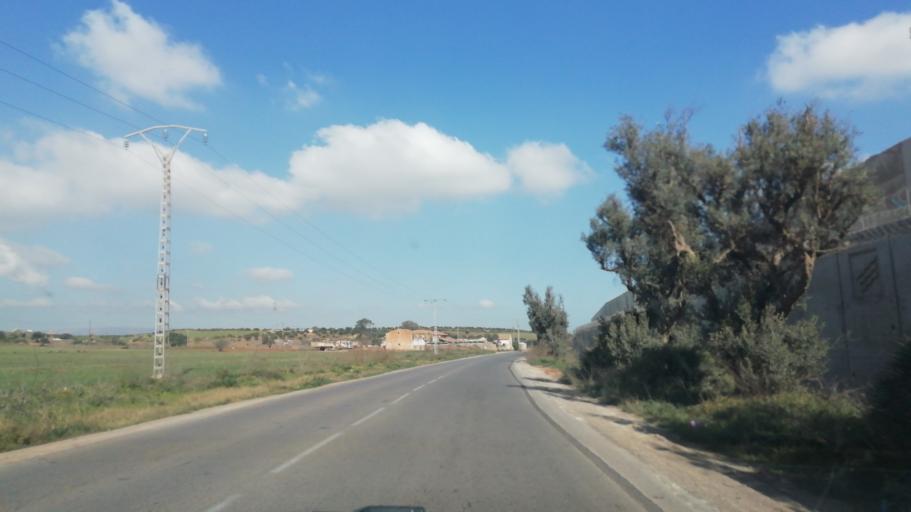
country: DZ
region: Oran
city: Ain el Bya
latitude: 35.7590
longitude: -0.2749
